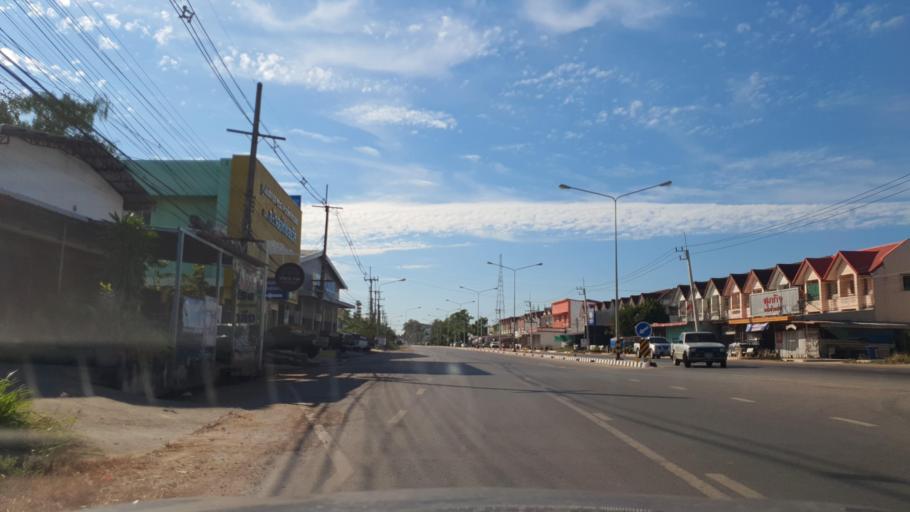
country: TH
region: Kalasin
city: Kuchinarai
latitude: 16.5379
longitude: 104.0622
